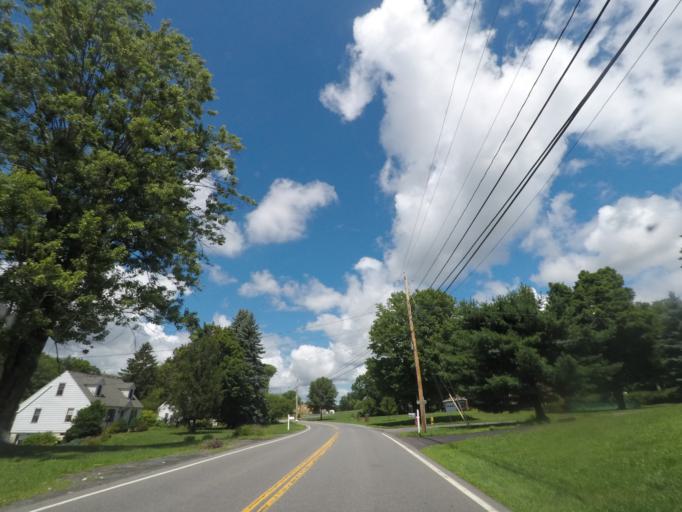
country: US
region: New York
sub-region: Rensselaer County
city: Wynantskill
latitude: 42.6840
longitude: -73.6809
